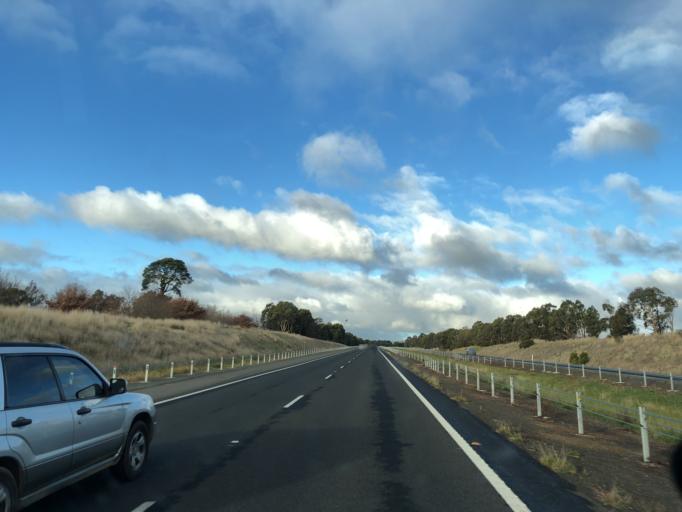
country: AU
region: Victoria
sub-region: Mount Alexander
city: Castlemaine
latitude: -37.2250
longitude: 144.4271
